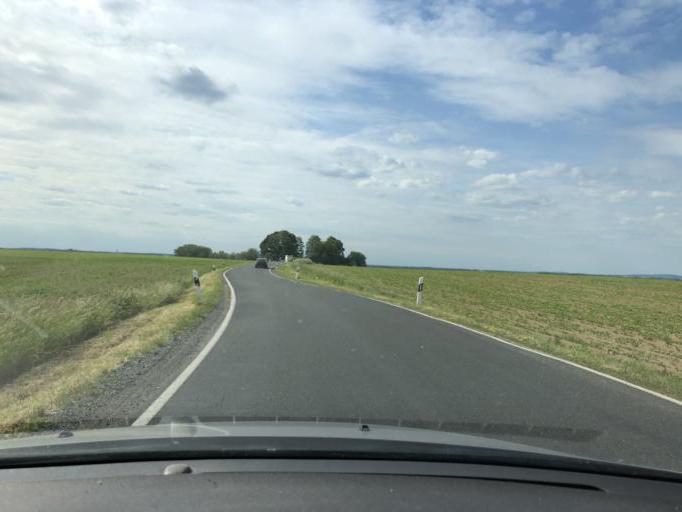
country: DE
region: Saxony
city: Nerchau
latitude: 51.2561
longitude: 12.8030
